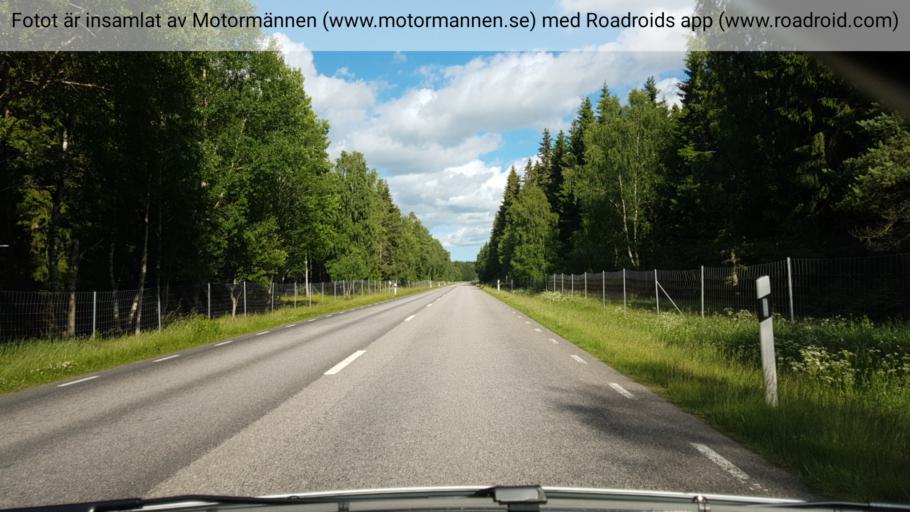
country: SE
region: Vaestra Goetaland
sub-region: Falkopings Kommun
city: Floby
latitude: 58.2076
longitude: 13.2842
